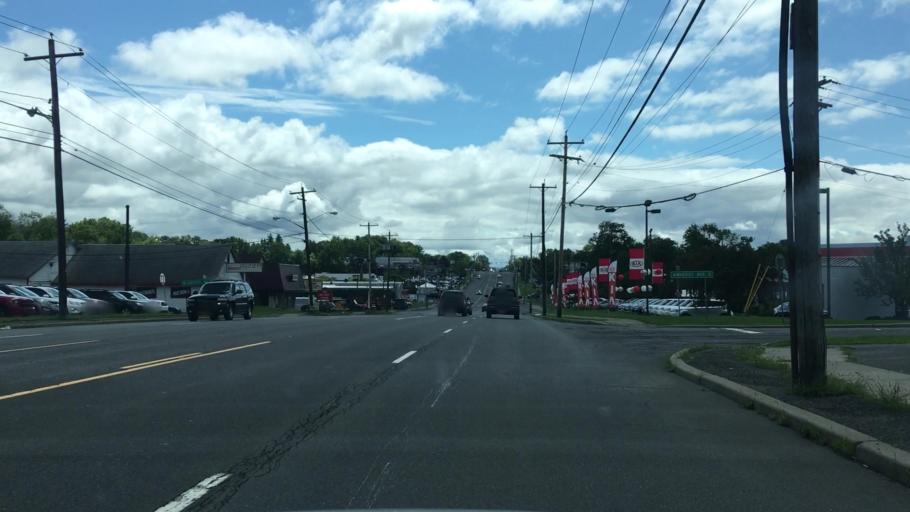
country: US
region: New York
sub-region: Schenectady County
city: Niskayuna
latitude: 42.7680
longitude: -73.8903
